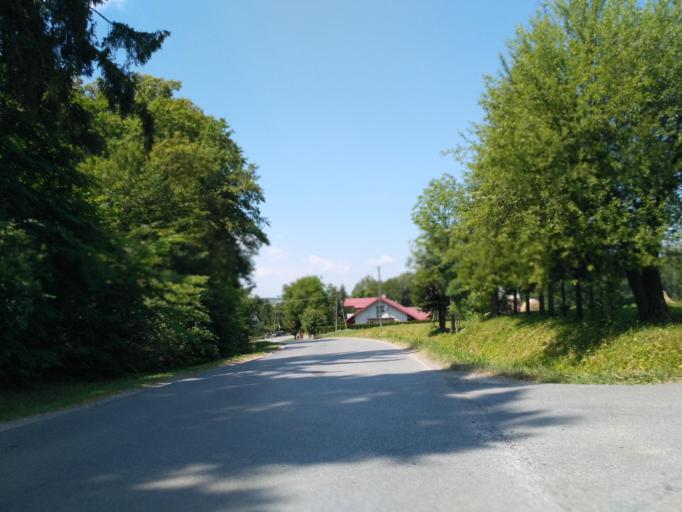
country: PL
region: Subcarpathian Voivodeship
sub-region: Powiat sanocki
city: Niebieszczany
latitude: 49.5098
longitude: 22.1504
